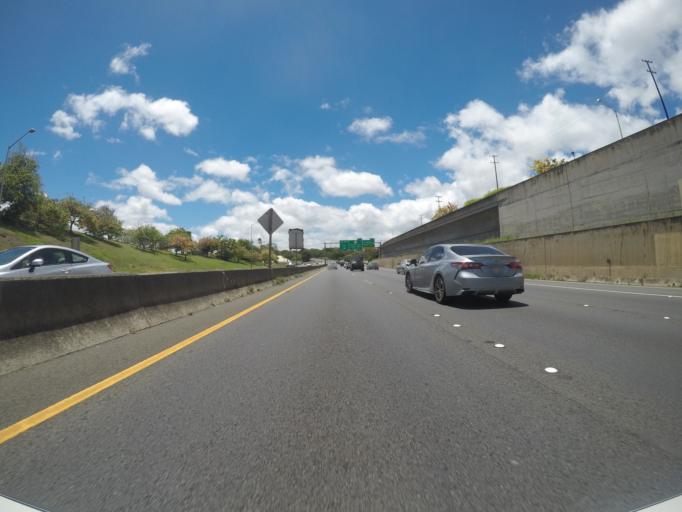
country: US
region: Hawaii
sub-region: Honolulu County
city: Honolulu
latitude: 21.3390
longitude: -157.8846
